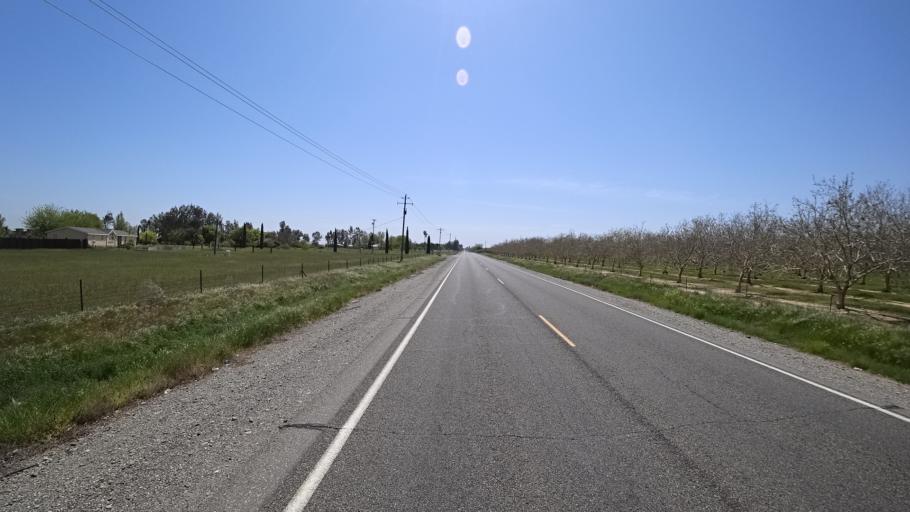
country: US
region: California
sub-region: Glenn County
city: Orland
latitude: 39.6414
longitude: -122.1973
